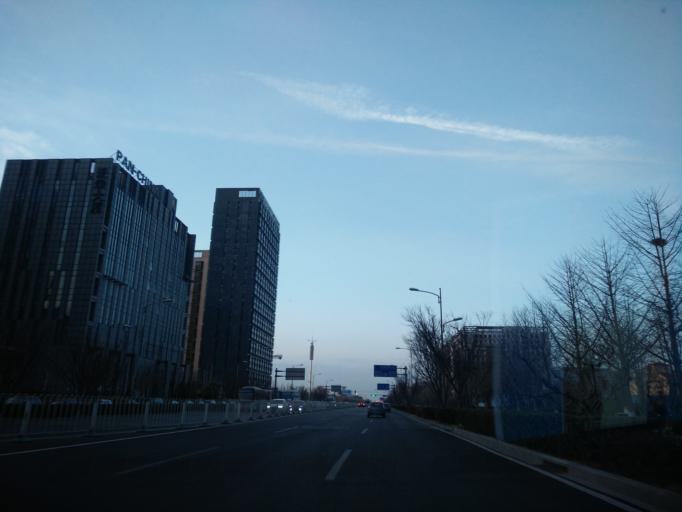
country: CN
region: Beijing
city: Jiugong
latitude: 39.7786
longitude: 116.5134
